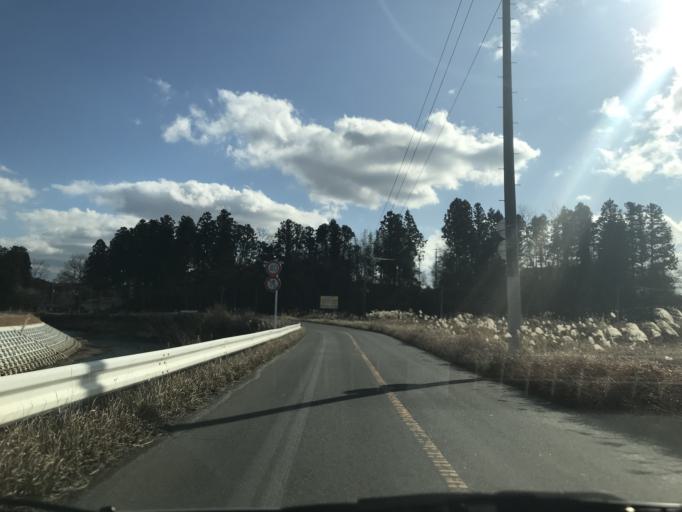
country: JP
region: Miyagi
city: Kogota
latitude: 38.7220
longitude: 141.0653
